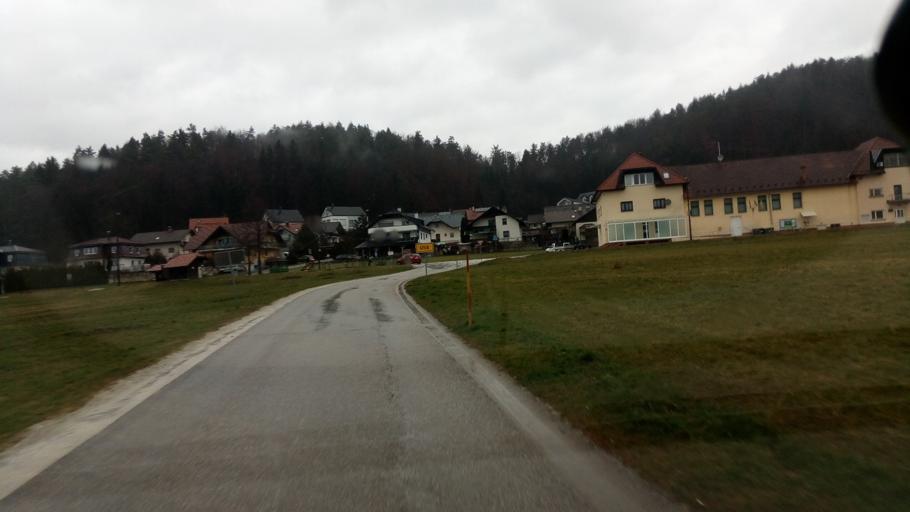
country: SI
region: Vodice
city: Vodice
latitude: 46.1680
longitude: 14.5150
